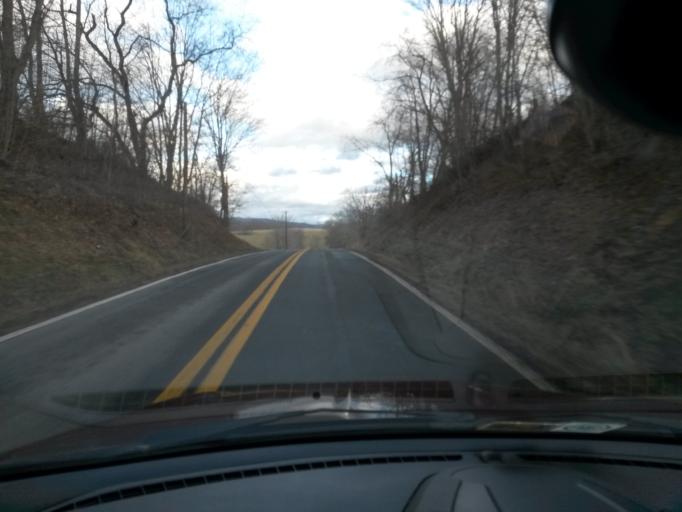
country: US
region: West Virginia
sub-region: Monroe County
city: Union
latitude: 37.5867
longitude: -80.4798
